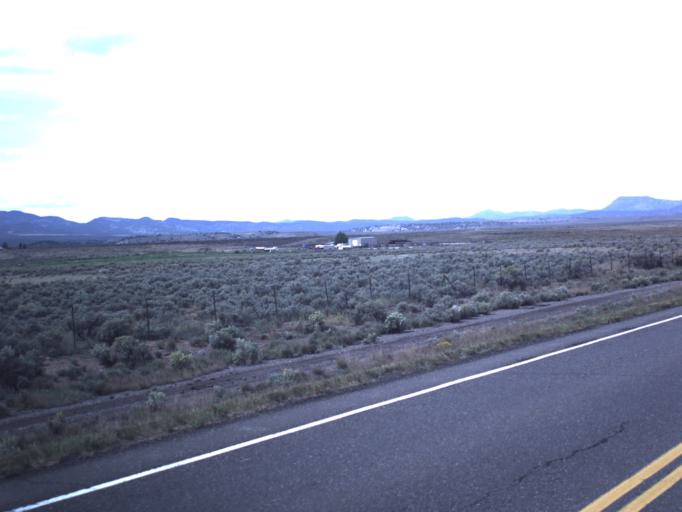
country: US
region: Utah
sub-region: Garfield County
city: Panguitch
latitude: 37.8825
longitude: -112.4367
